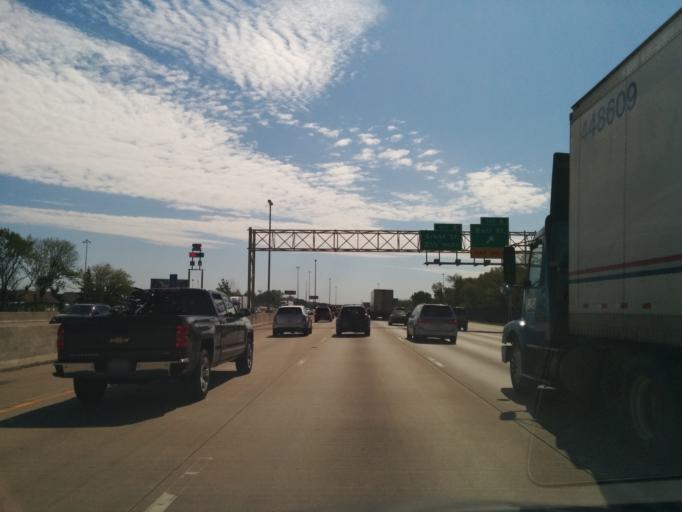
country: US
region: Indiana
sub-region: Lake County
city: Griffith
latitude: 41.5698
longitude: -87.4102
